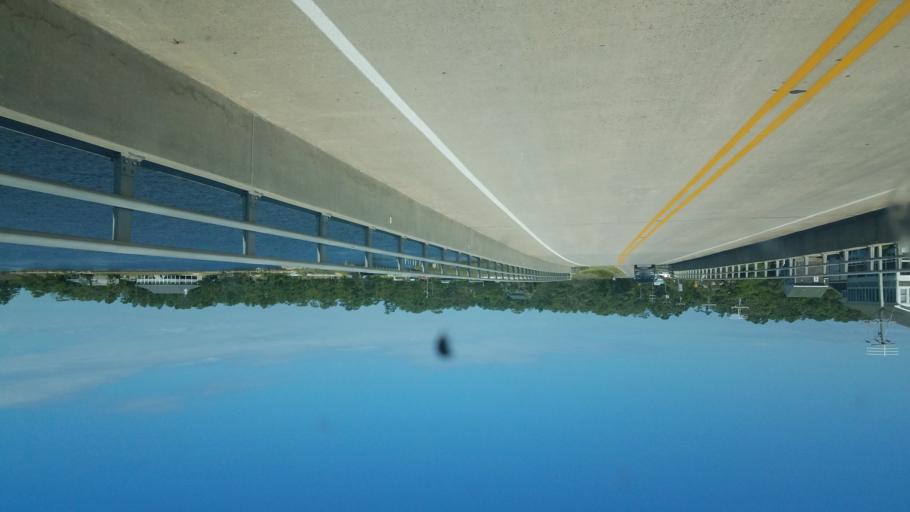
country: US
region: North Carolina
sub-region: Dare County
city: Kill Devil Hills
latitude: 36.0154
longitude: -75.6869
